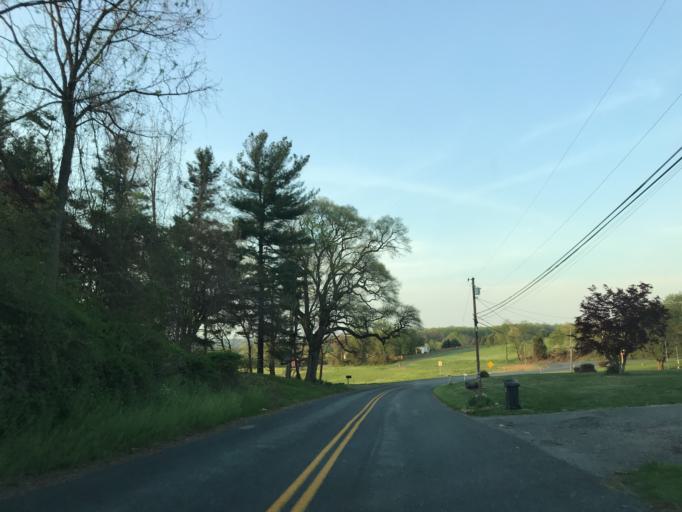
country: US
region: Maryland
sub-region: Harford County
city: Jarrettsville
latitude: 39.6048
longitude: -76.4139
